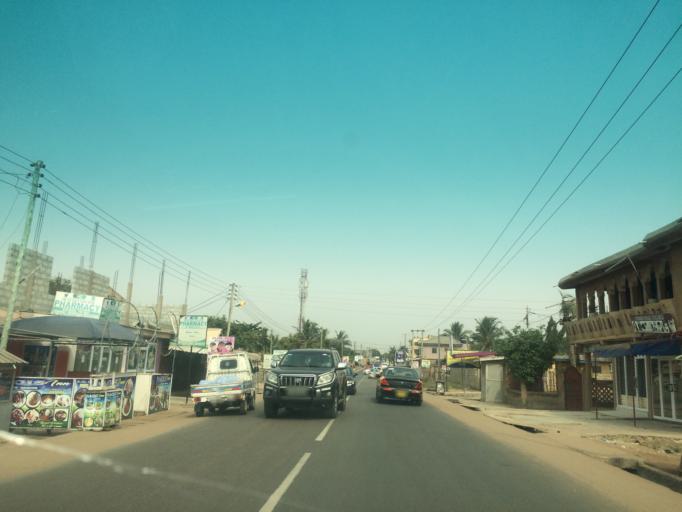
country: GH
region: Greater Accra
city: Nungua
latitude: 5.6092
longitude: -0.0868
